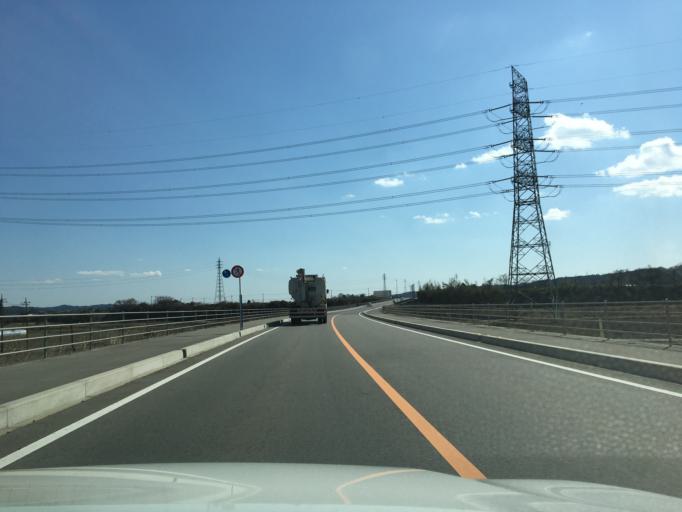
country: JP
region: Tochigi
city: Otawara
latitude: 36.7882
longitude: 140.1165
